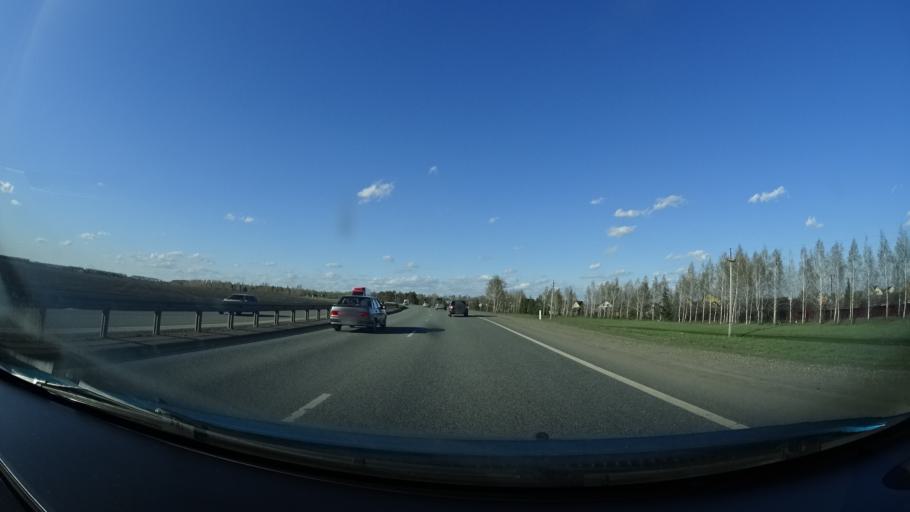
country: RU
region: Bashkortostan
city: Ufa
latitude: 54.5539
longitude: 55.9243
